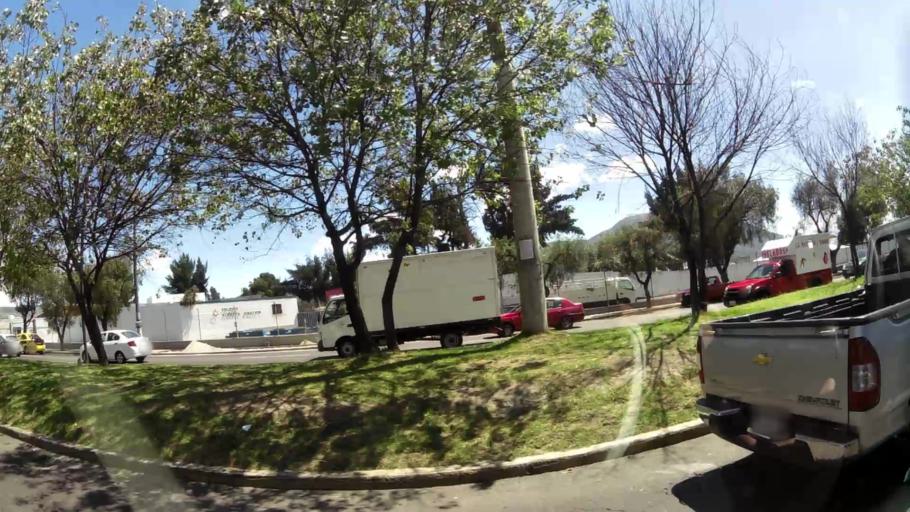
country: EC
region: Pichincha
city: Quito
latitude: -0.0924
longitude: -78.4781
